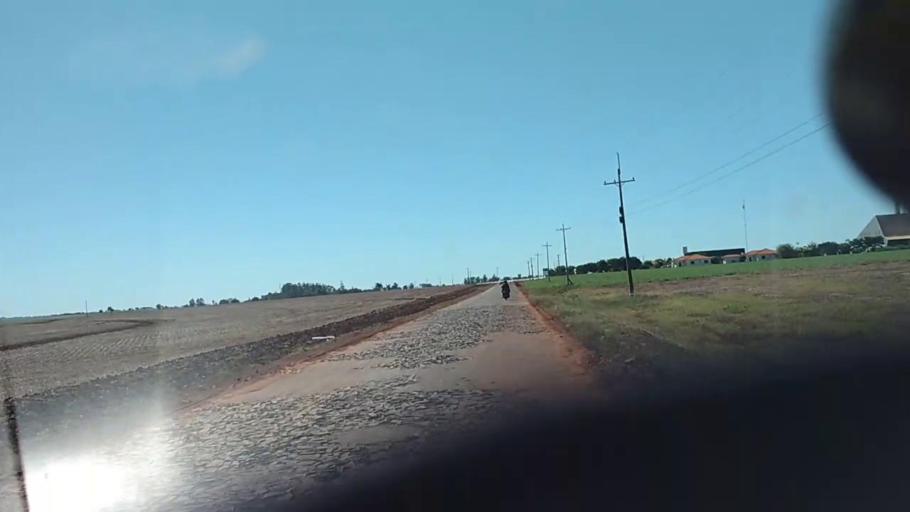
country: PY
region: Alto Parana
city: Naranjal
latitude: -25.9725
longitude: -55.1534
